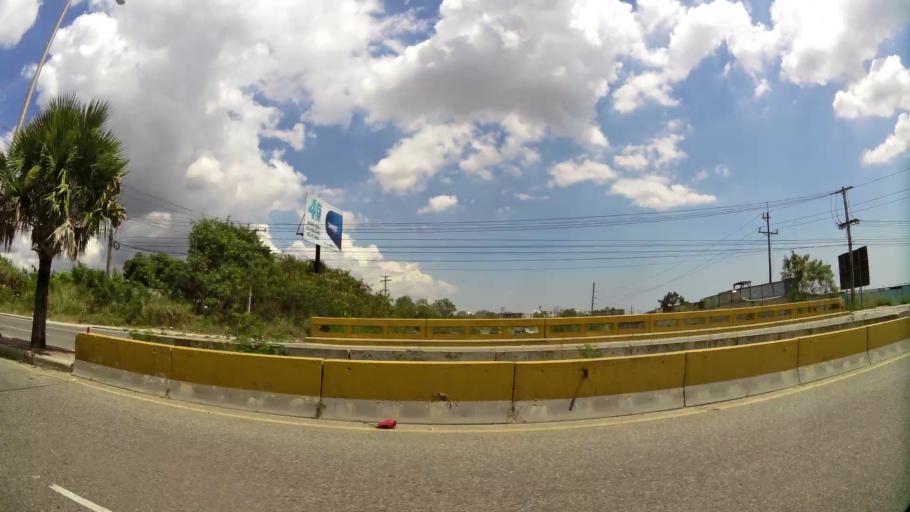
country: DO
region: Nacional
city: La Agustina
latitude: 18.5536
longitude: -69.9447
